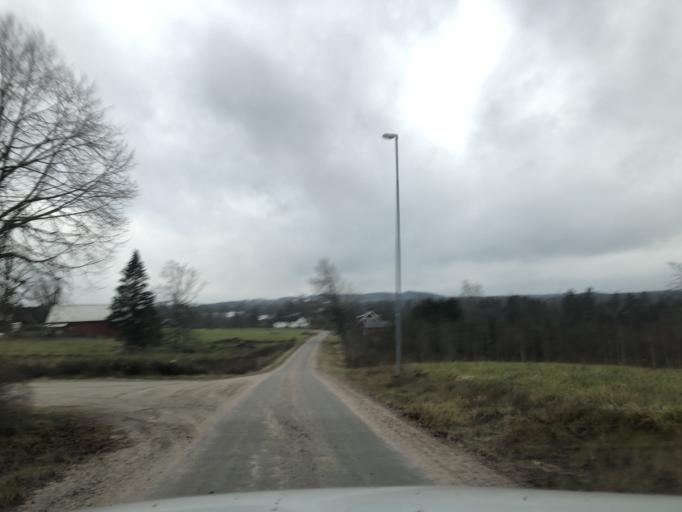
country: SE
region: Vaestra Goetaland
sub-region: Ulricehamns Kommun
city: Ulricehamn
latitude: 57.8674
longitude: 13.5554
